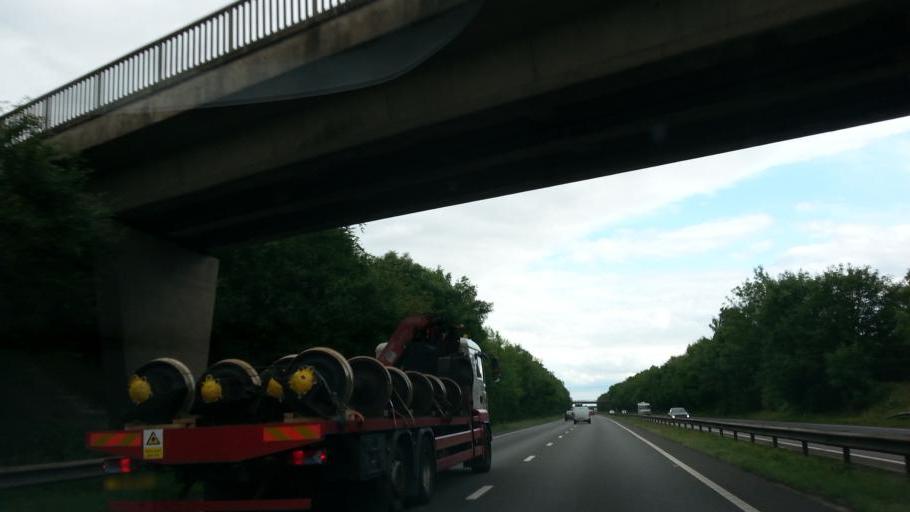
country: GB
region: England
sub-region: Nottinghamshire
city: Tuxford
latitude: 53.2079
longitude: -0.8681
